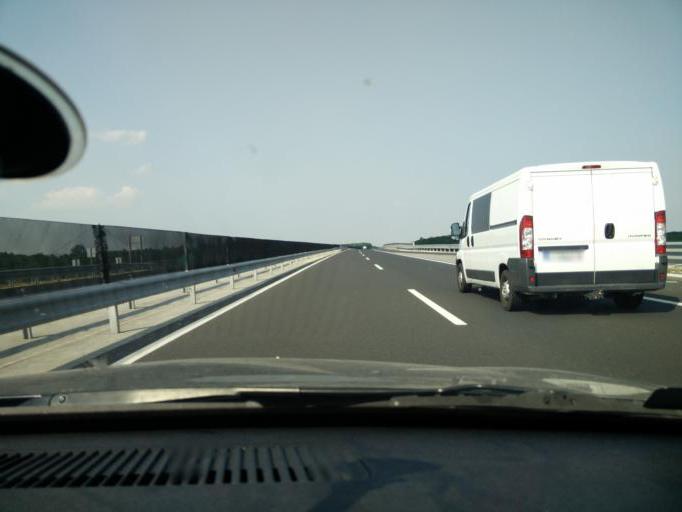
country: HU
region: Tolna
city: Szedres
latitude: 46.4707
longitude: 18.7189
